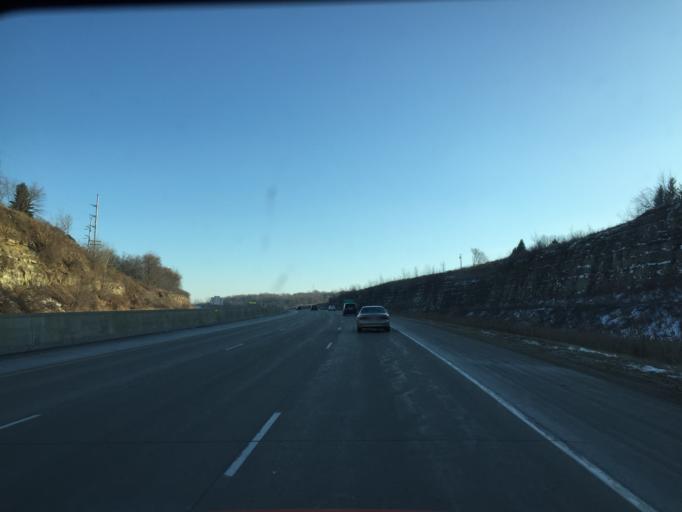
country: US
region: Minnesota
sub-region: Olmsted County
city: Rochester
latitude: 43.9871
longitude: -92.4790
